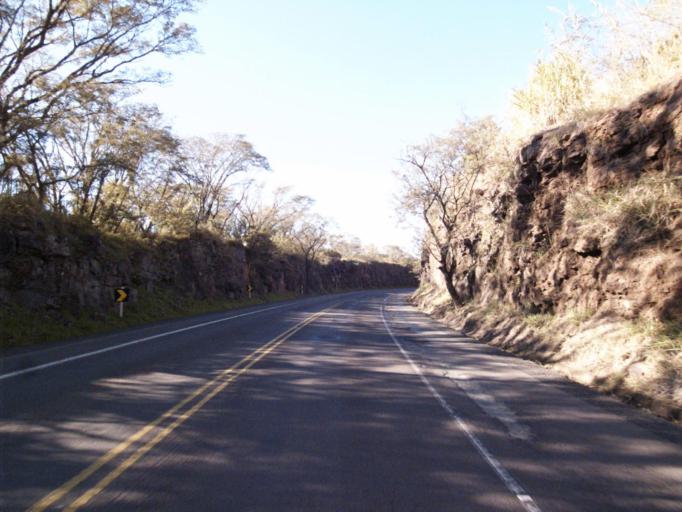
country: BR
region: Rio Grande do Sul
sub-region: Frederico Westphalen
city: Frederico Westphalen
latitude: -26.8045
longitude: -53.4423
